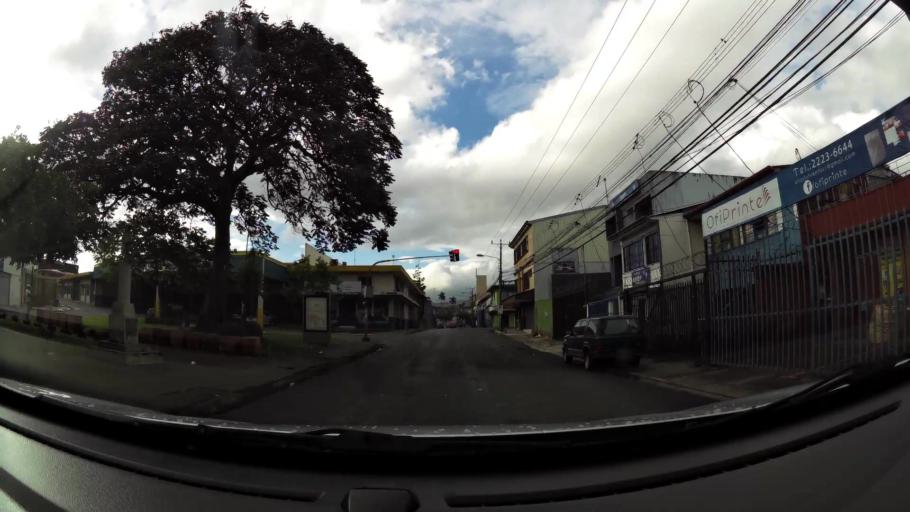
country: CR
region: San Jose
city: San Jose
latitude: 9.9385
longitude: -84.0871
